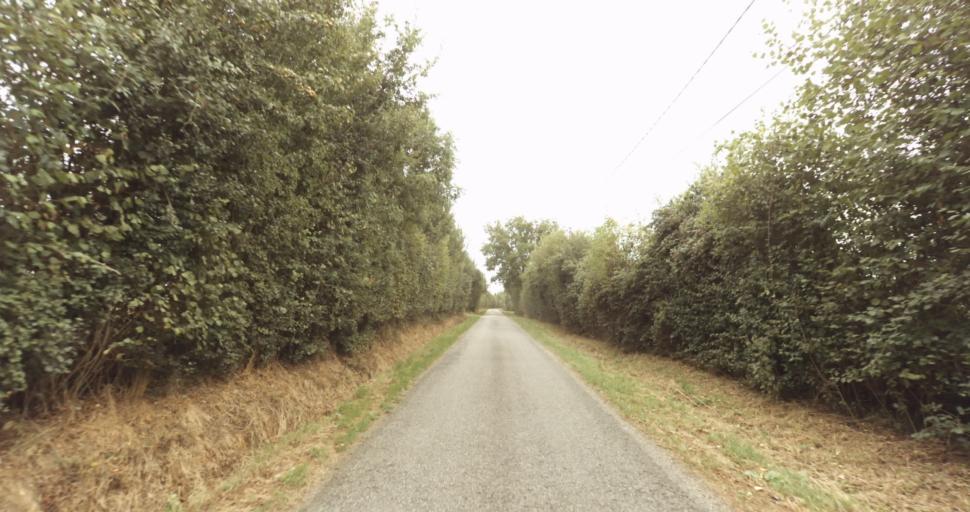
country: FR
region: Lower Normandy
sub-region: Departement de l'Orne
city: Sainte-Gauburge-Sainte-Colombe
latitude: 48.7224
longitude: 0.4605
